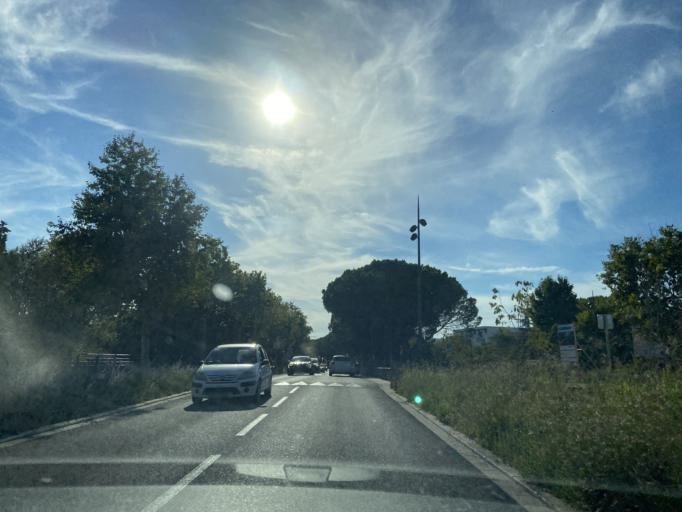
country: FR
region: Provence-Alpes-Cote d'Azur
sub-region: Departement des Bouches-du-Rhone
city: Miramas
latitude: 43.5882
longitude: 4.9980
